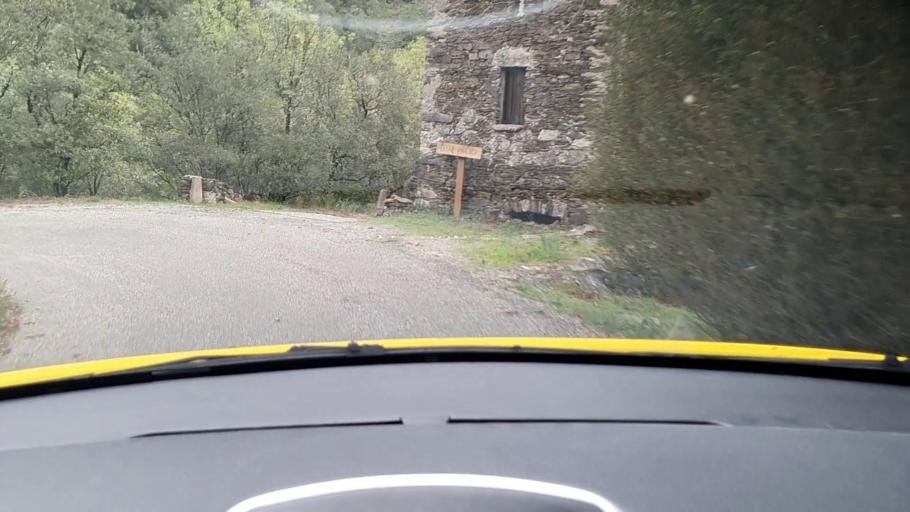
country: FR
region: Languedoc-Roussillon
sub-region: Departement du Gard
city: Sumene
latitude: 44.0144
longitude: 3.6612
